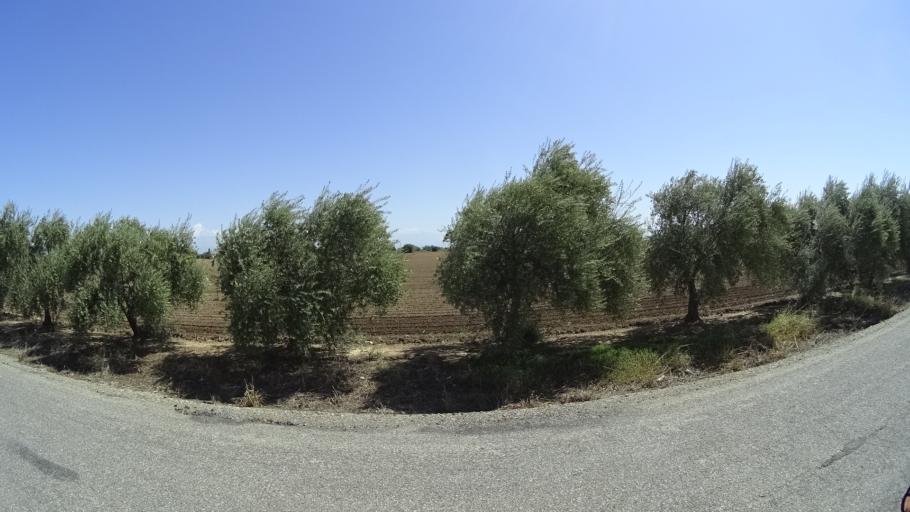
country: US
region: California
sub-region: Glenn County
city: Orland
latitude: 39.7777
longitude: -122.1690
